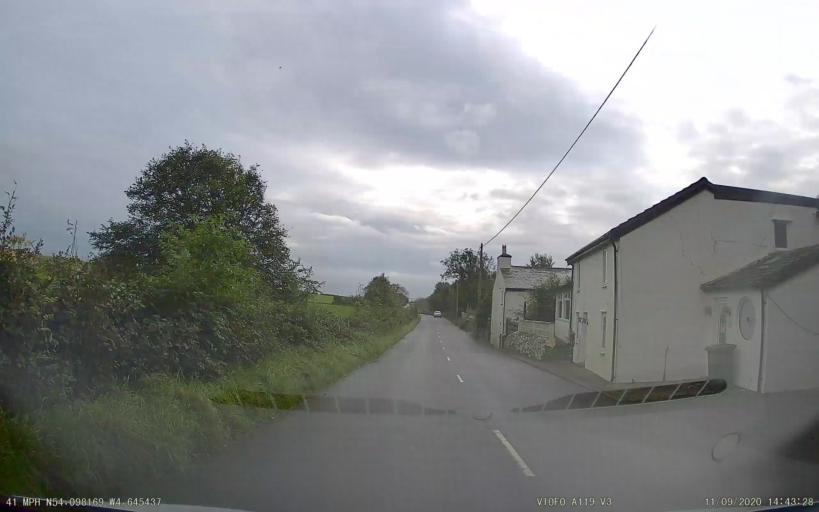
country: IM
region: Castletown
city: Castletown
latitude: 54.0982
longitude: -4.6454
